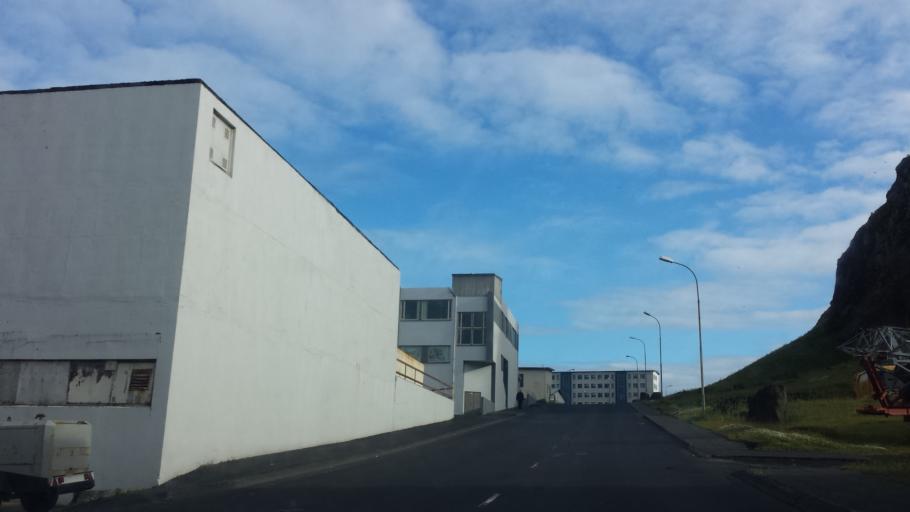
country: IS
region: South
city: Vestmannaeyjar
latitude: 63.4426
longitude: -20.2817
